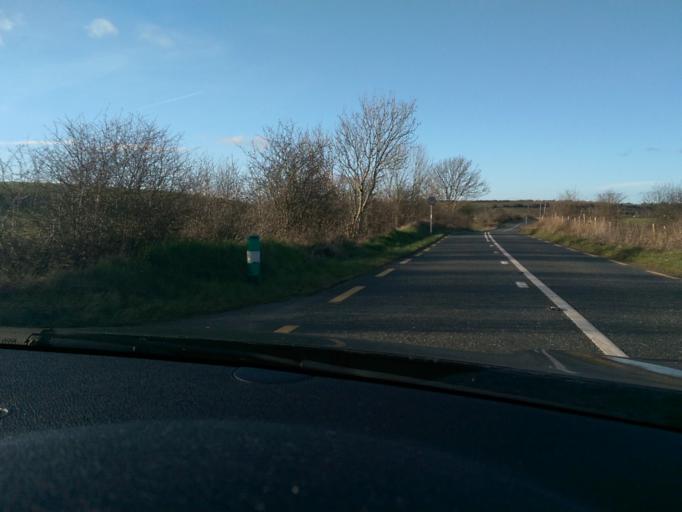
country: IE
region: Connaught
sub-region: Roscommon
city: Boyle
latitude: 53.9323
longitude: -8.2774
